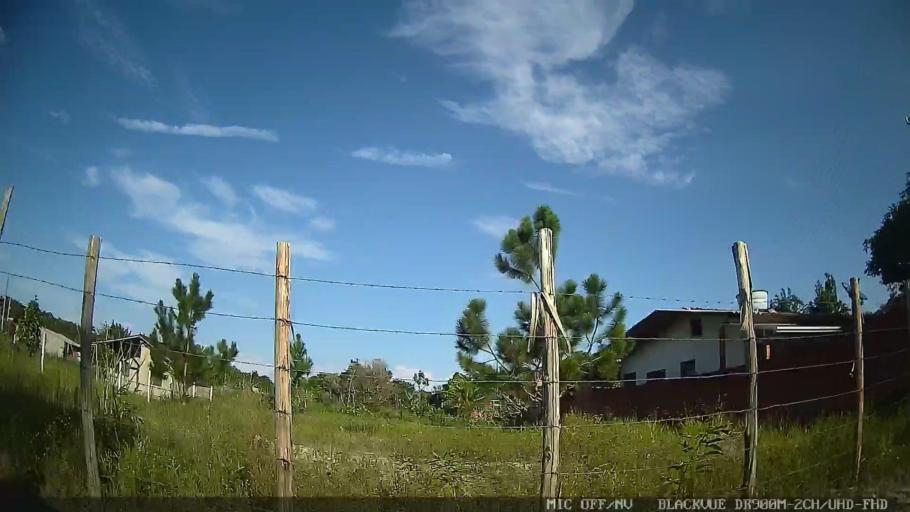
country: BR
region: Sao Paulo
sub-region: Itanhaem
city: Itanhaem
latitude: -24.1714
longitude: -46.8204
